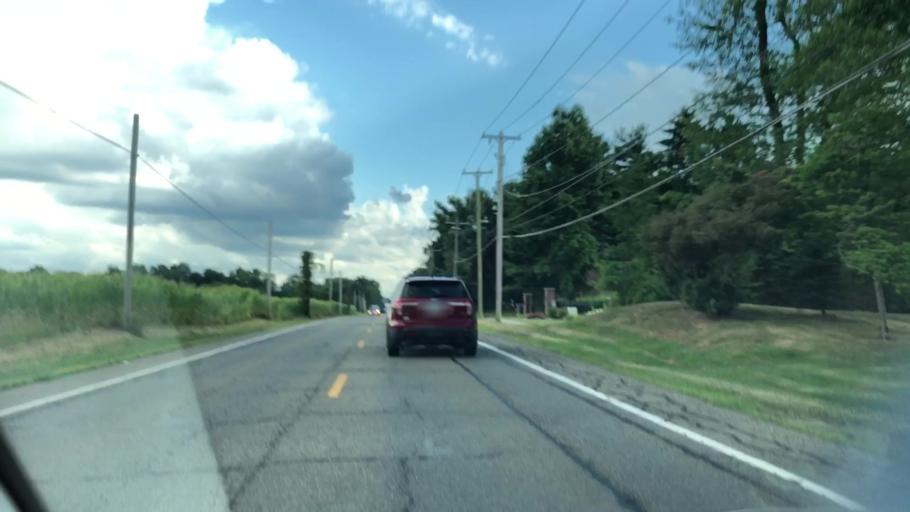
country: US
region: Ohio
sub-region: Summit County
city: Green
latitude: 40.9640
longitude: -81.4939
